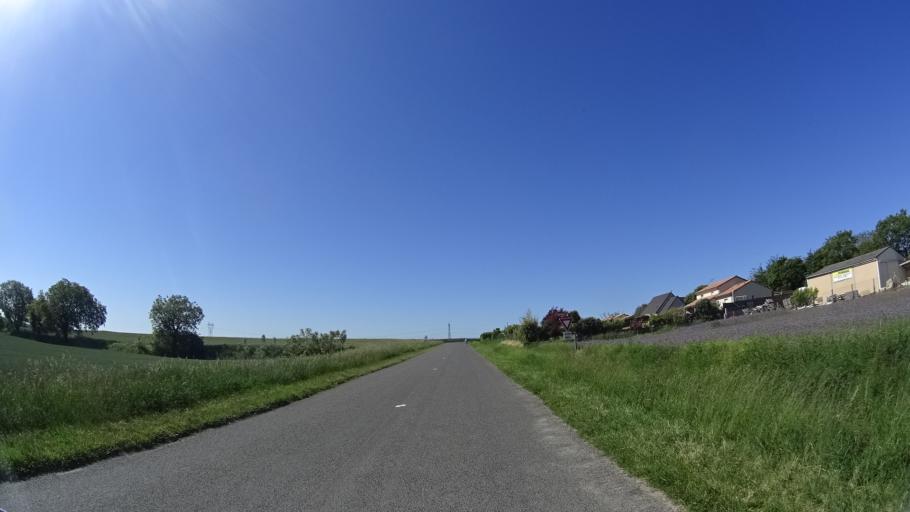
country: FR
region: Pays de la Loire
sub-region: Departement de Maine-et-Loire
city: Doue-la-Fontaine
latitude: 47.2336
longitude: -0.2917
